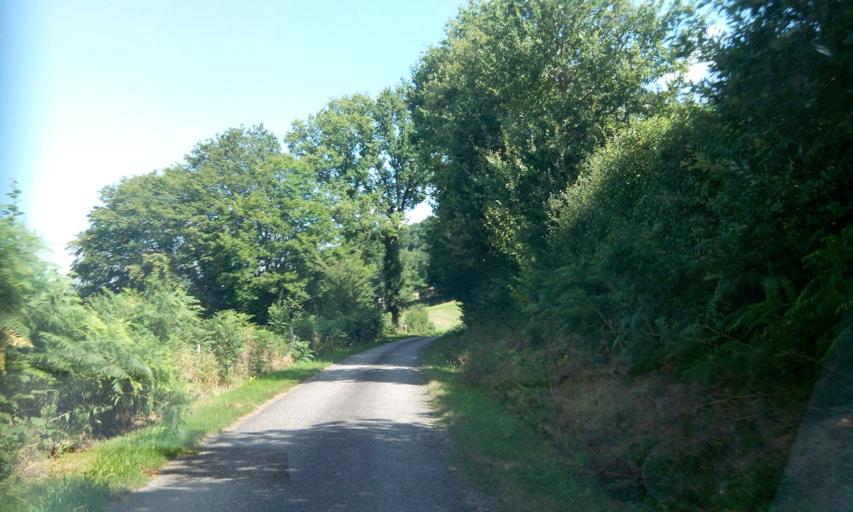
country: FR
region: Limousin
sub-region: Departement de la Haute-Vienne
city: Saint-Leonard-de-Noblat
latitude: 45.8077
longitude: 1.4794
